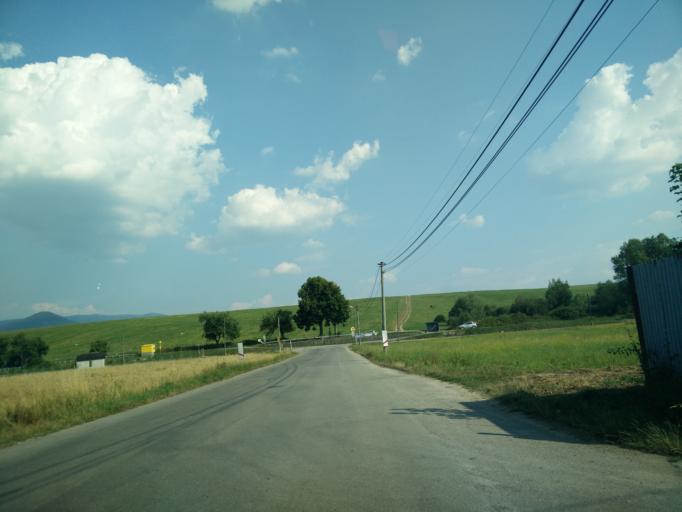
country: SK
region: Zilinsky
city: Rajec
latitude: 49.1177
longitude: 18.6541
